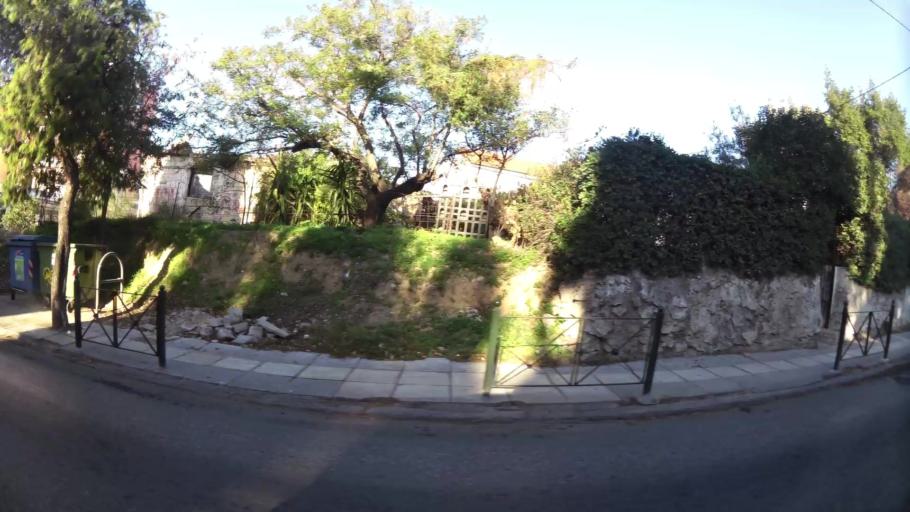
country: GR
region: Attica
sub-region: Nomarchia Athinas
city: Lykovrysi
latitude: 38.0625
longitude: 23.7749
